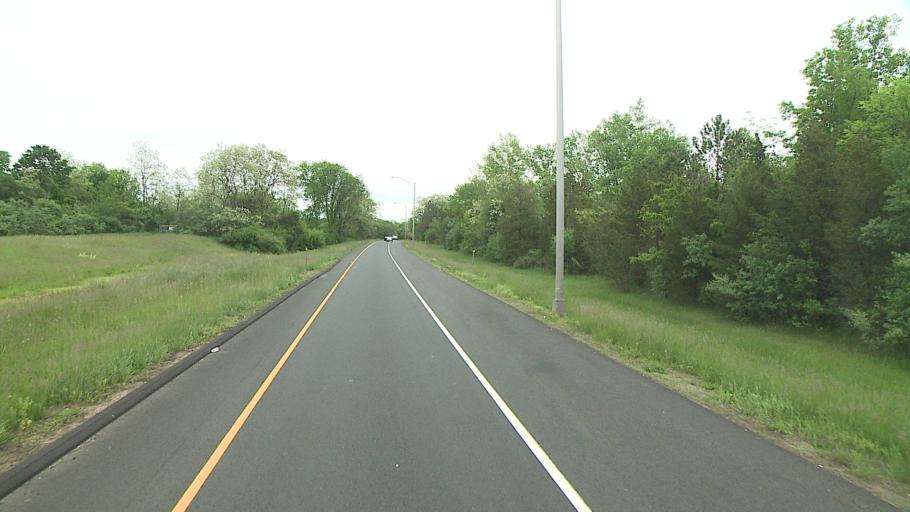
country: US
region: Connecticut
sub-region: Hartford County
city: West Hartford
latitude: 41.7253
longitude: -72.7766
